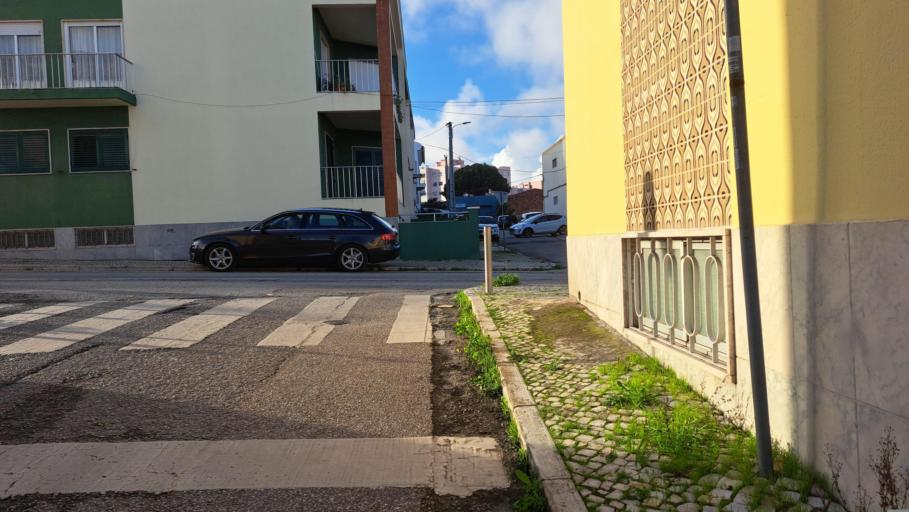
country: PT
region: Setubal
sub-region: Moita
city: Alhos Vedros
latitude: 38.6542
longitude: -9.0459
